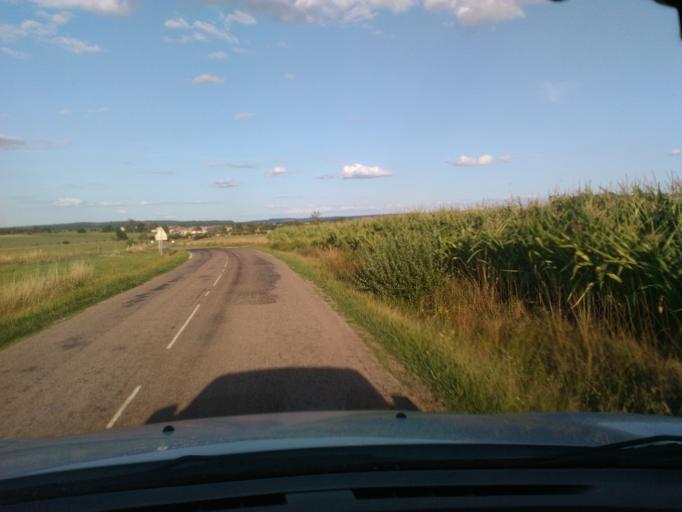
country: FR
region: Lorraine
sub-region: Departement des Vosges
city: Mirecourt
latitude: 48.3502
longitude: 6.0456
